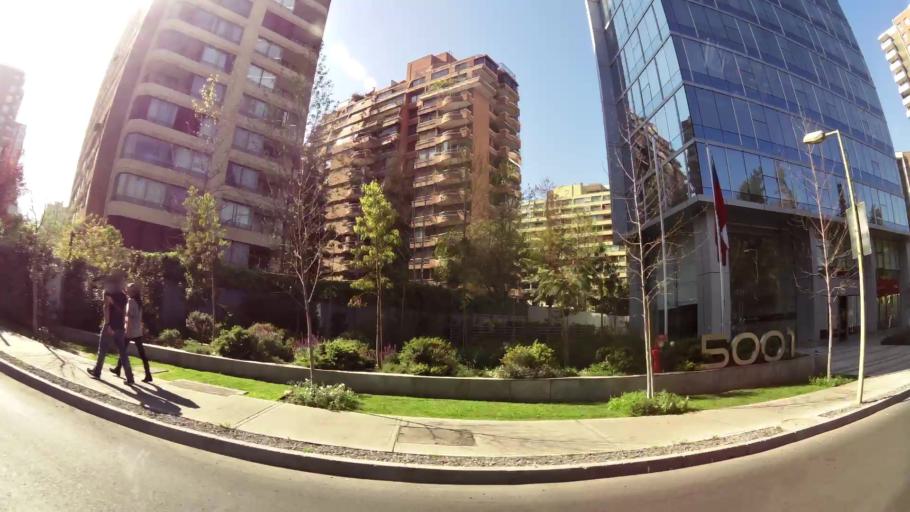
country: CL
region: Santiago Metropolitan
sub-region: Provincia de Santiago
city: Villa Presidente Frei, Nunoa, Santiago, Chile
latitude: -33.4093
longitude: -70.5778
